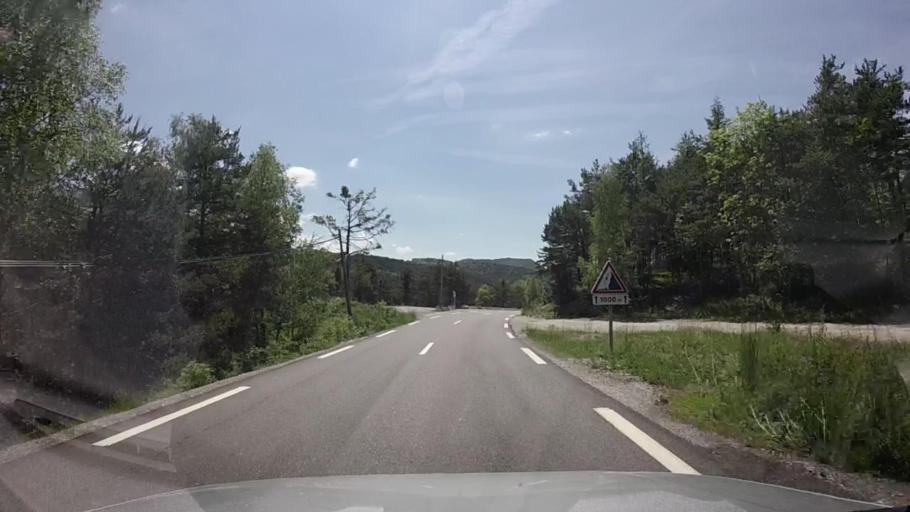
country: FR
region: Provence-Alpes-Cote d'Azur
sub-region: Departement des Alpes-de-Haute-Provence
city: Seyne-les-Alpes
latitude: 44.3968
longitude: 6.3343
